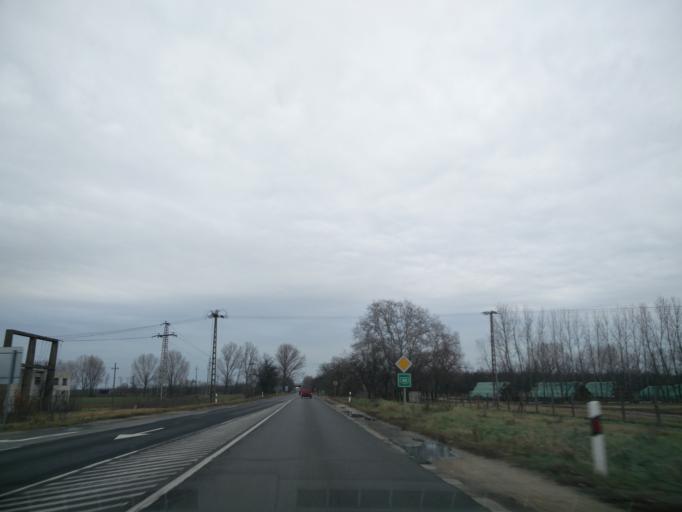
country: HU
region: Pest
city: Vecses
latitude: 47.4002
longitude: 19.2966
